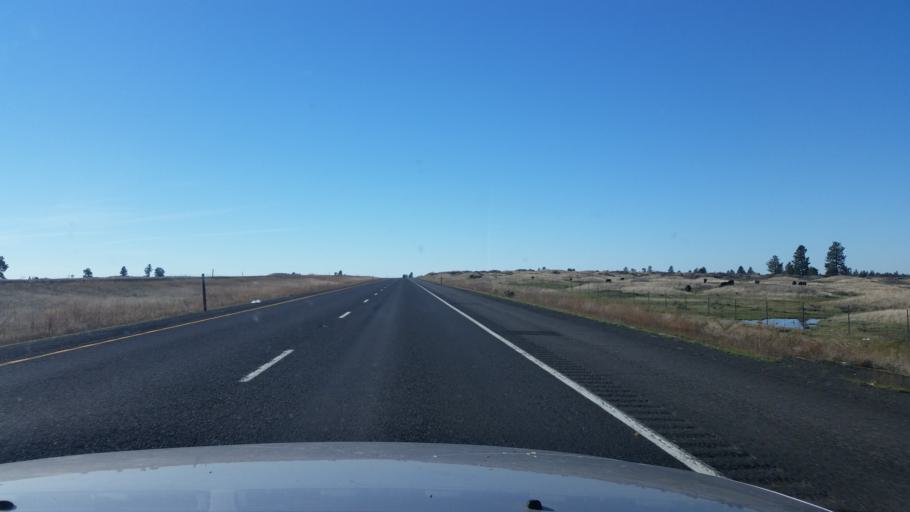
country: US
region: Washington
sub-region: Spokane County
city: Medical Lake
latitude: 47.3894
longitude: -117.8516
